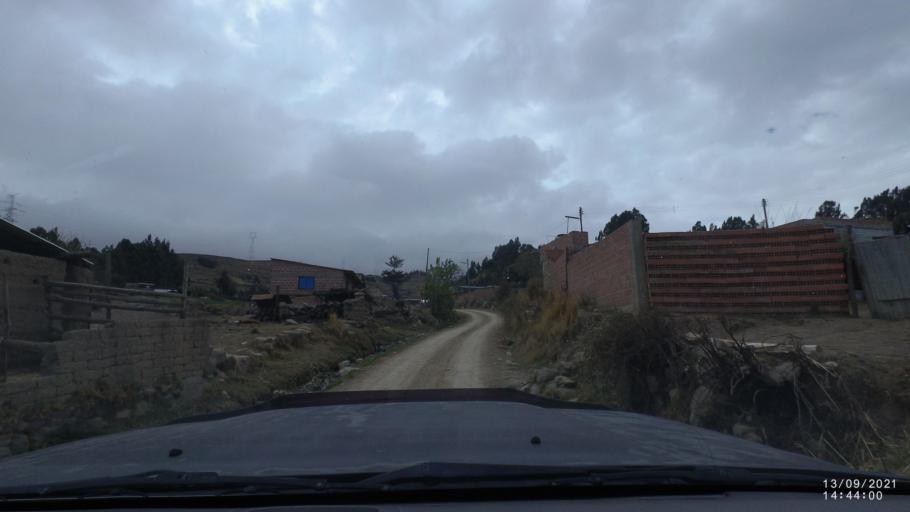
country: BO
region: Cochabamba
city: Colomi
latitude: -17.3607
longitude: -65.8119
